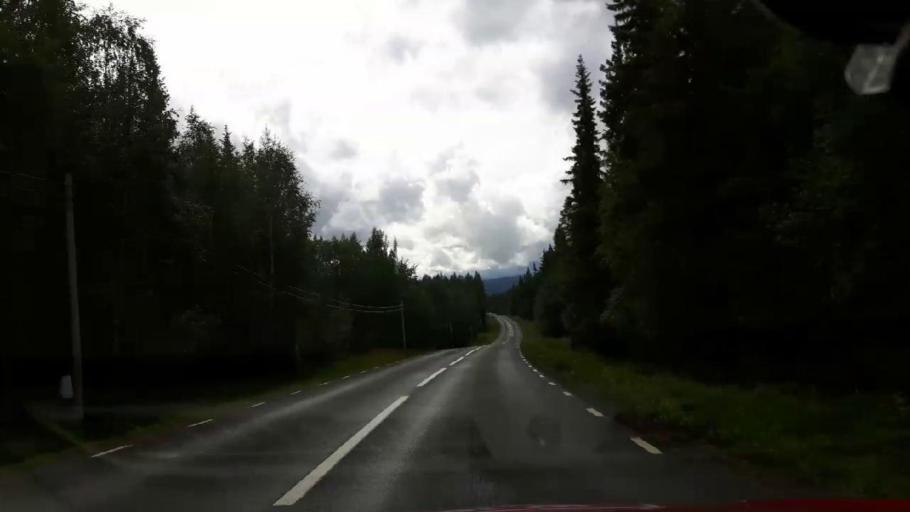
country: NO
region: Nord-Trondelag
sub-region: Lierne
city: Sandvika
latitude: 64.5178
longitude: 14.1612
